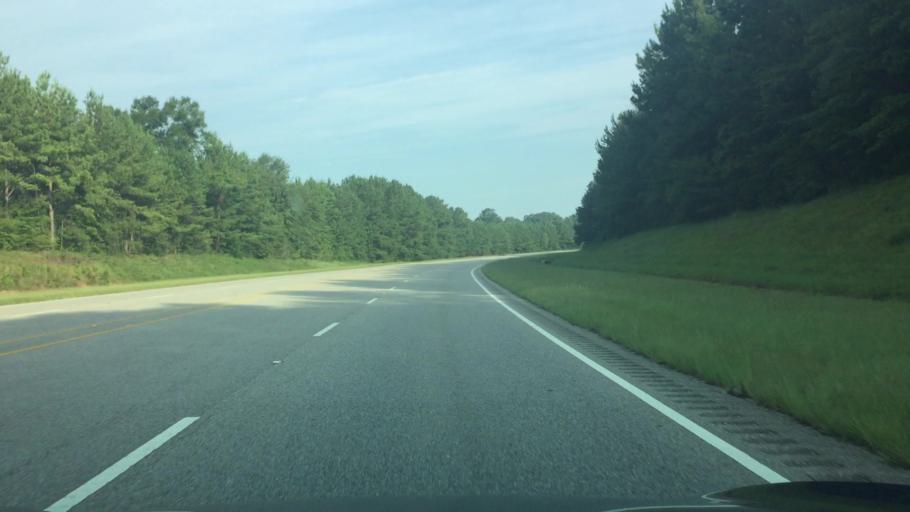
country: US
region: Alabama
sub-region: Butler County
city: Georgiana
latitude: 31.4676
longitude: -86.6625
